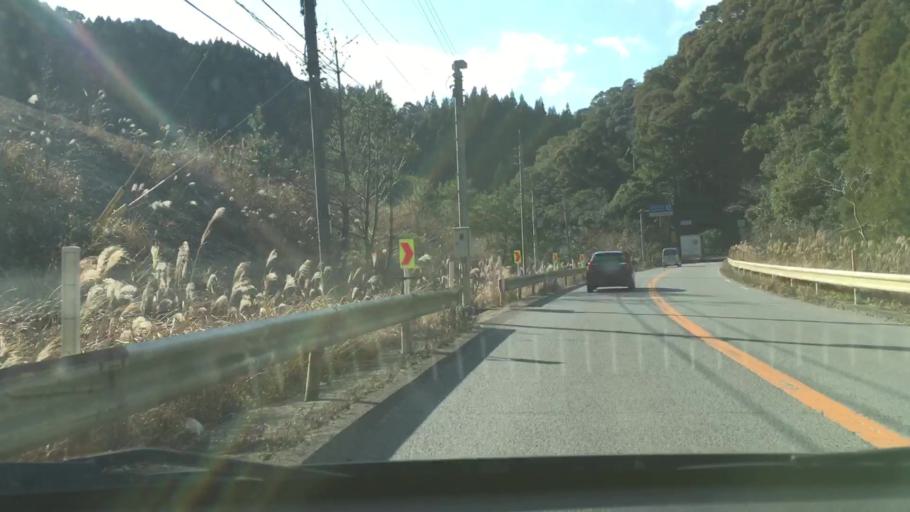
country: JP
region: Oita
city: Tsukumiura
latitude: 33.0033
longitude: 131.7938
